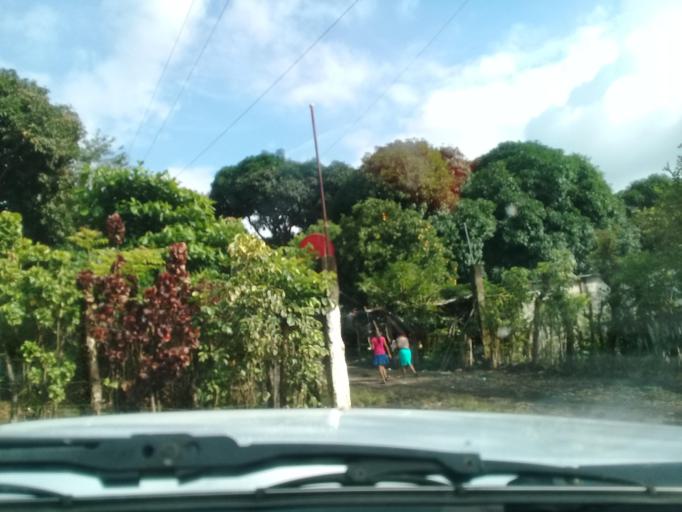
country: MX
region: Veracruz
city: Catemaco
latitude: 18.4340
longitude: -95.1292
